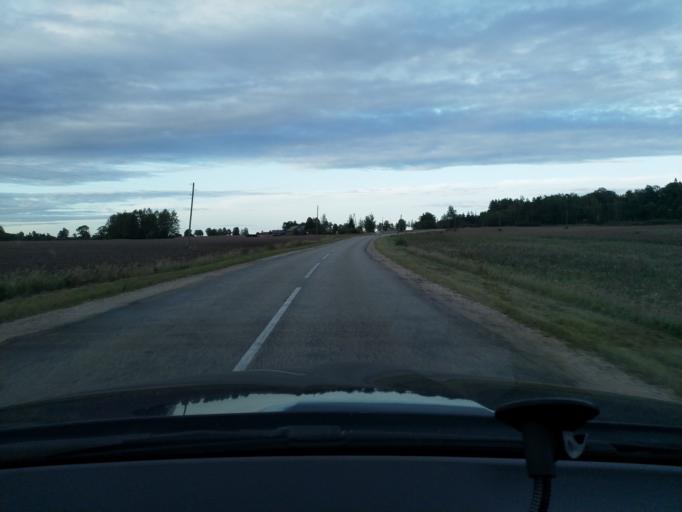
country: LV
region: Talsu Rajons
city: Sabile
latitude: 56.9331
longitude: 22.5708
